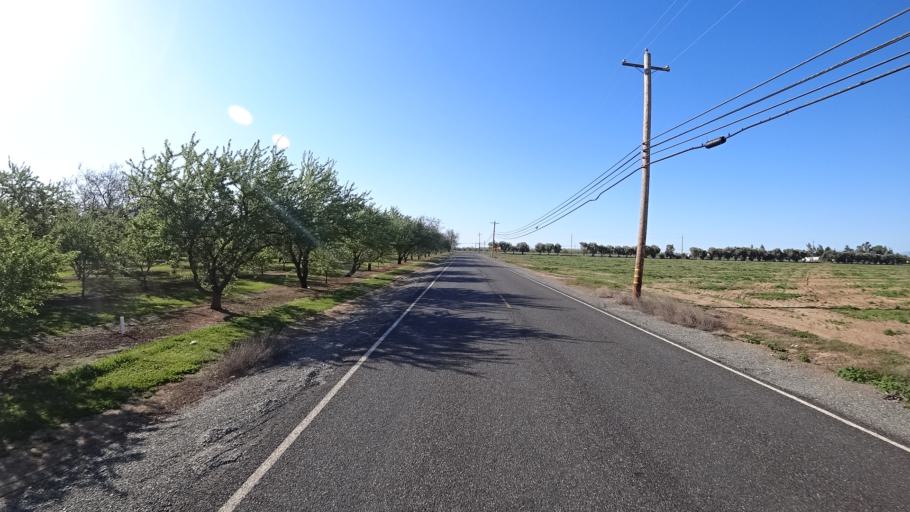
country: US
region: California
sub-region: Glenn County
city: Hamilton City
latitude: 39.7701
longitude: -122.1042
